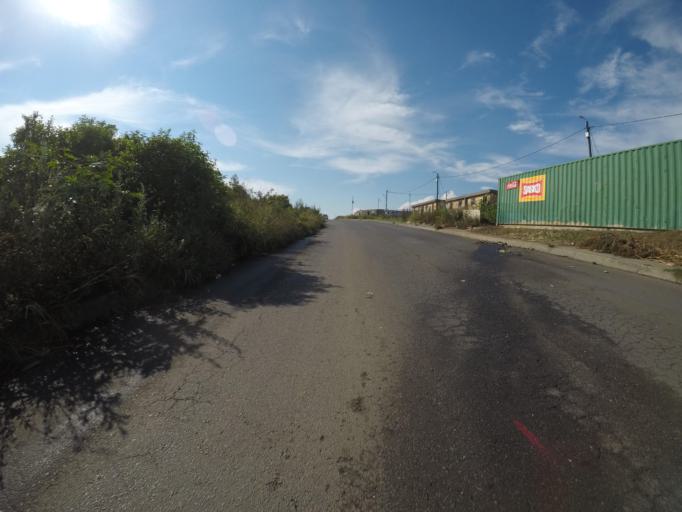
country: ZA
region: Eastern Cape
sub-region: Buffalo City Metropolitan Municipality
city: East London
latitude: -33.0078
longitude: 27.8573
